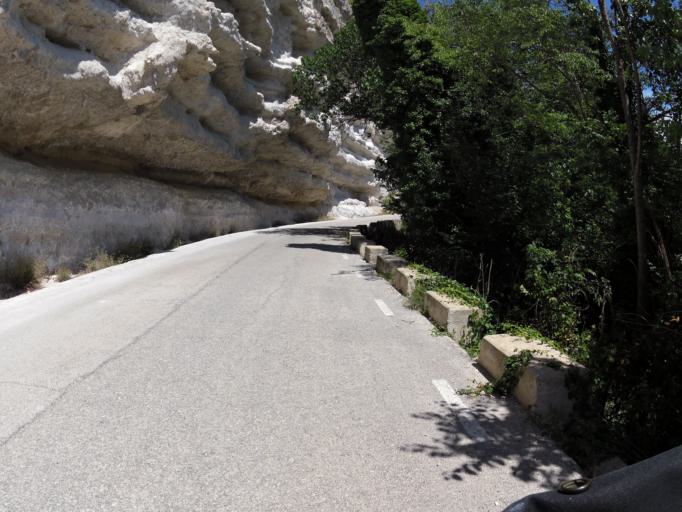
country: ES
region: Castille-La Mancha
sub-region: Provincia de Albacete
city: Jorquera
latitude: 39.1795
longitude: -1.5312
